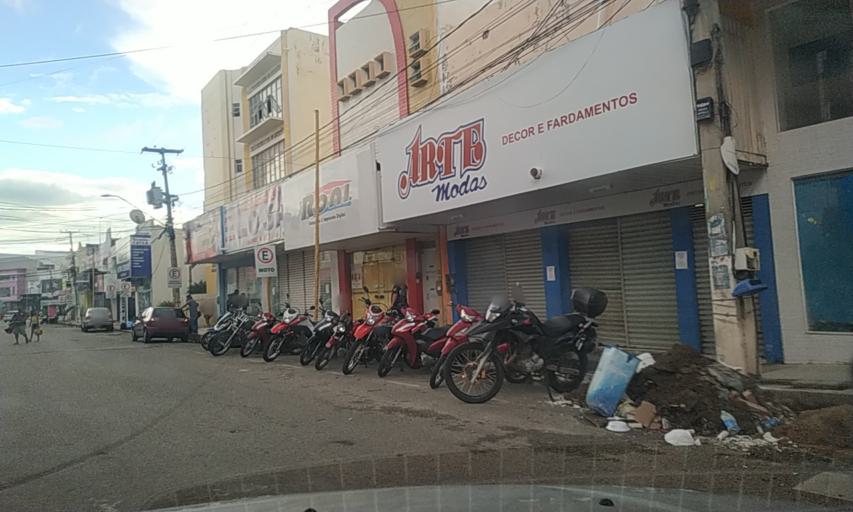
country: BR
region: Rio Grande do Norte
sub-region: Mossoro
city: Mossoro
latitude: -5.1928
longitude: -37.3420
